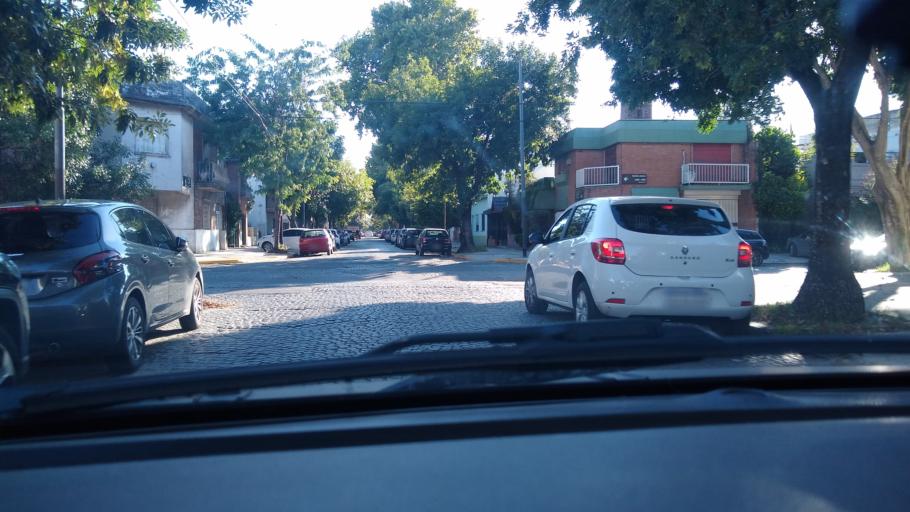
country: AR
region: Buenos Aires F.D.
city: Villa Santa Rita
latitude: -34.6093
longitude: -58.5149
